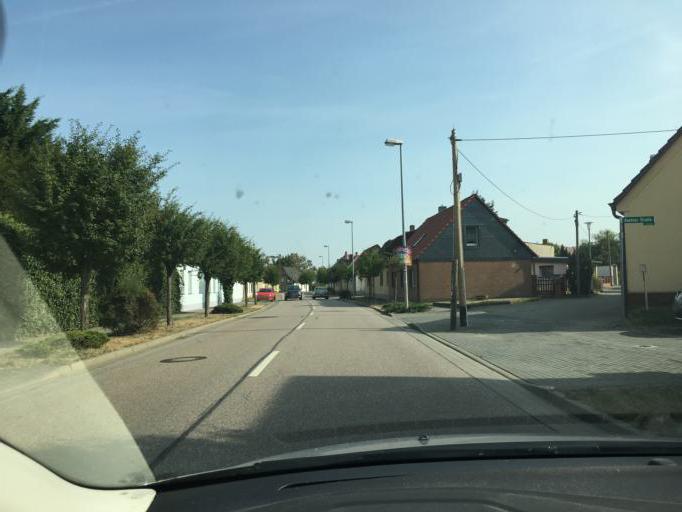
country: DE
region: Saxony-Anhalt
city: Wulfen
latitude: 51.7826
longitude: 11.8871
